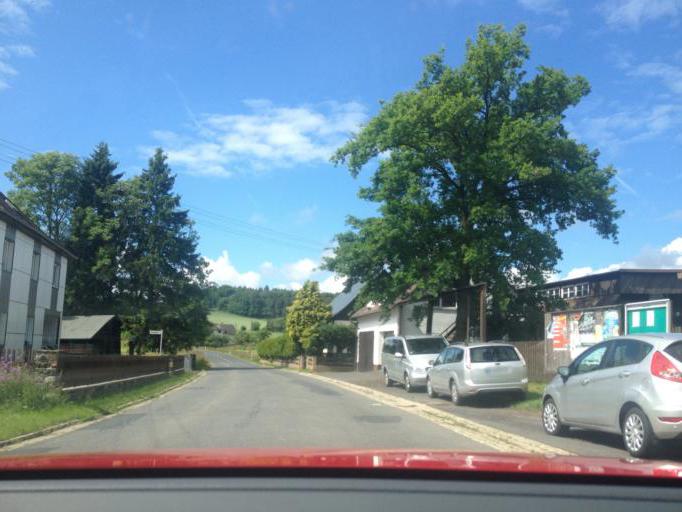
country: DE
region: Bavaria
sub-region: Upper Palatinate
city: Pechbrunn
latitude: 50.0054
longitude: 12.1963
